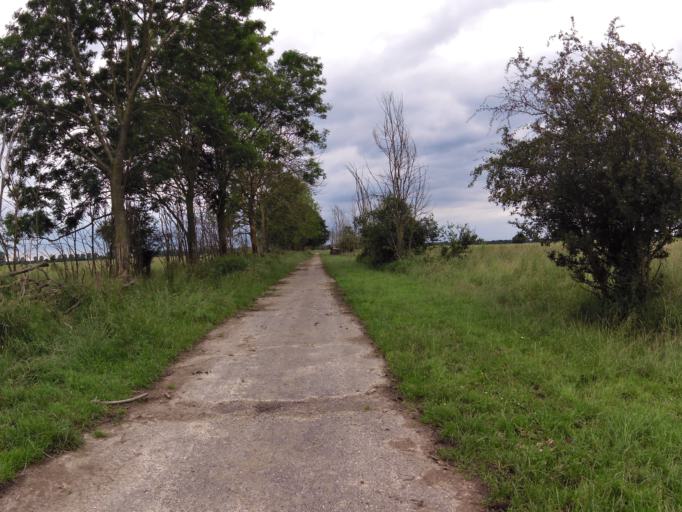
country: NL
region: North Brabant
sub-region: Gemeente Landerd
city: Reek
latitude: 51.7645
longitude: 5.6904
